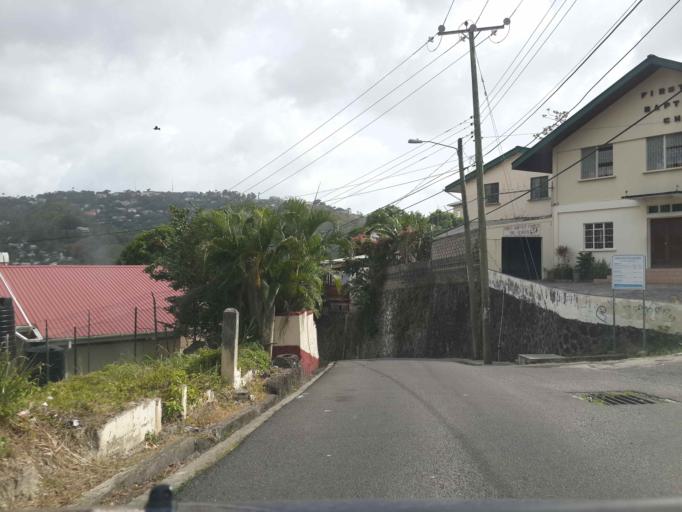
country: LC
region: Castries Quarter
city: Bisee
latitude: 14.0151
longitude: -60.9875
